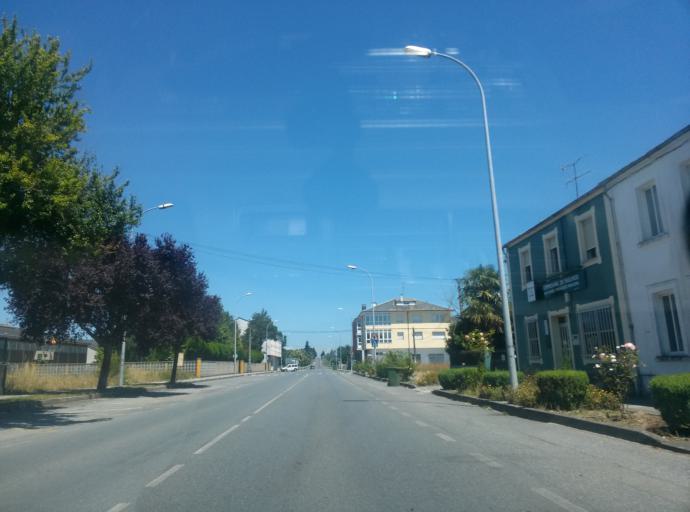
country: ES
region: Galicia
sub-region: Provincia de Lugo
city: Mos
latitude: 43.1475
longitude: -7.4903
